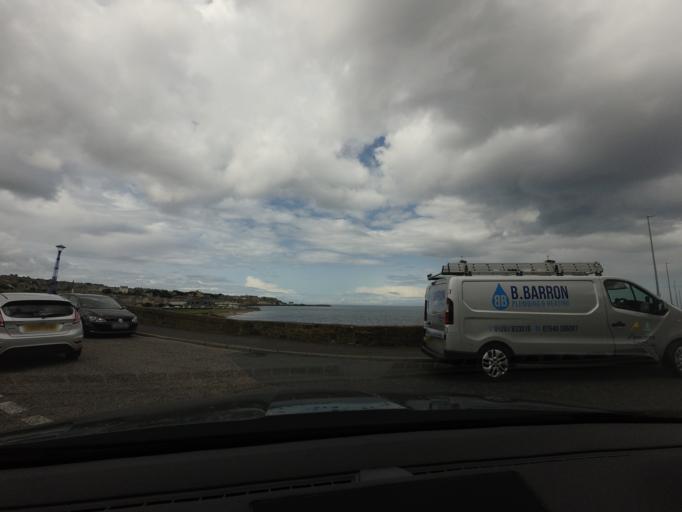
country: GB
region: Scotland
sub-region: Aberdeenshire
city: Macduff
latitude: 57.6629
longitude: -2.5120
